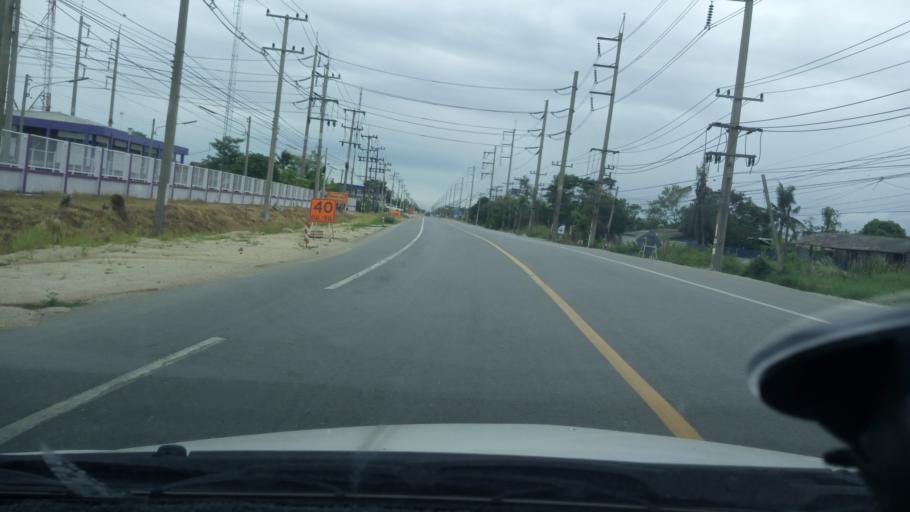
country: TH
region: Chon Buri
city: Phanat Nikhom
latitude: 13.4944
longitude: 101.1647
